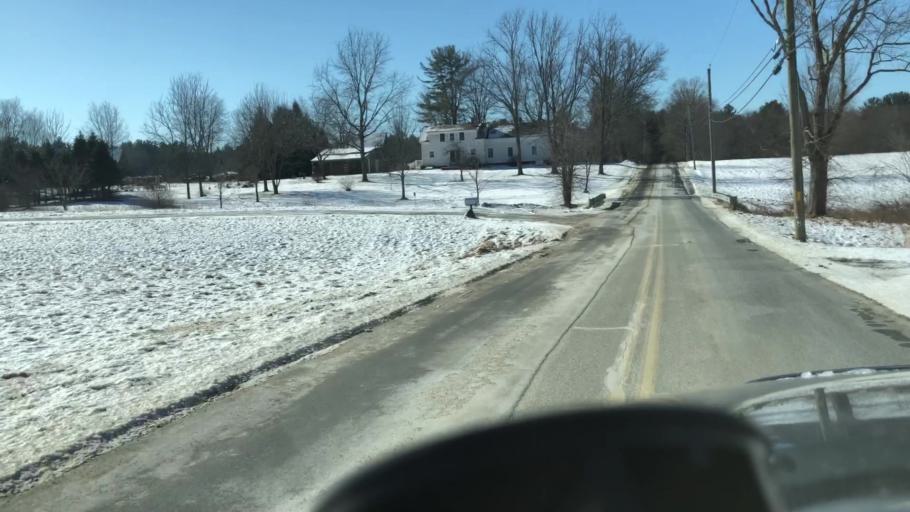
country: US
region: Massachusetts
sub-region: Hampshire County
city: Southampton
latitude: 42.2259
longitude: -72.7080
